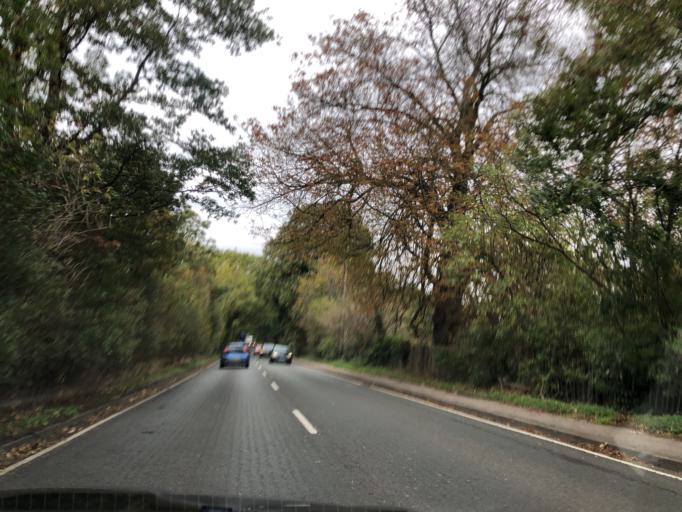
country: GB
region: England
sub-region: Warwickshire
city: Royal Leamington Spa
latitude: 52.3057
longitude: -1.5379
